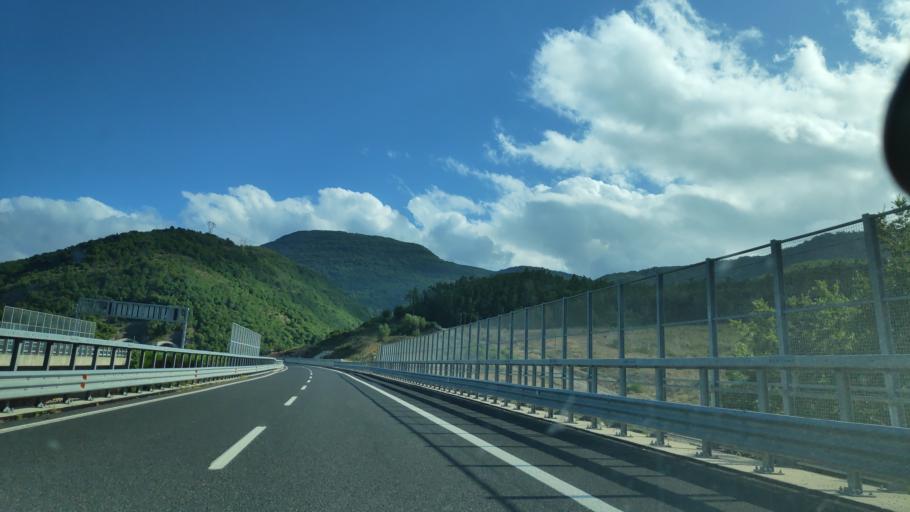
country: IT
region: Campania
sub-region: Provincia di Salerno
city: Casalbuono
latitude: 40.2196
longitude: 15.6717
